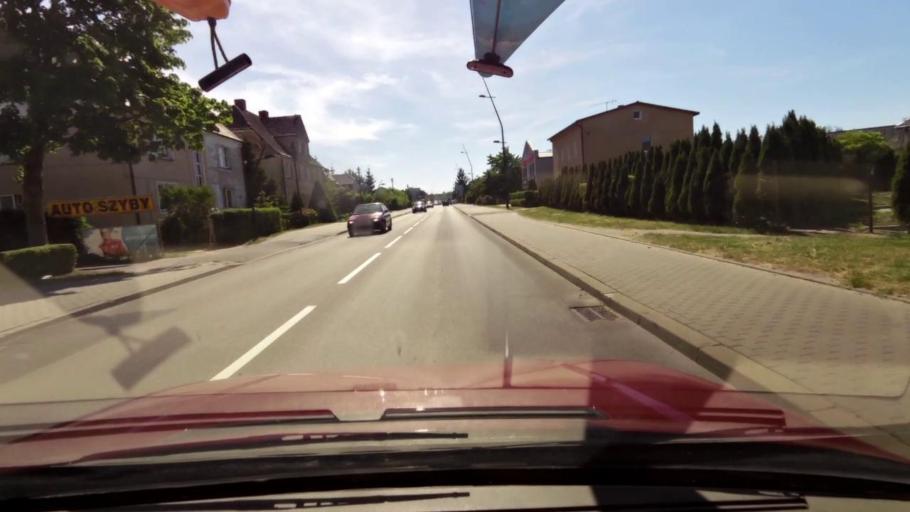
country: PL
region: Pomeranian Voivodeship
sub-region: Powiat slupski
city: Kobylnica
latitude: 54.4455
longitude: 17.0051
